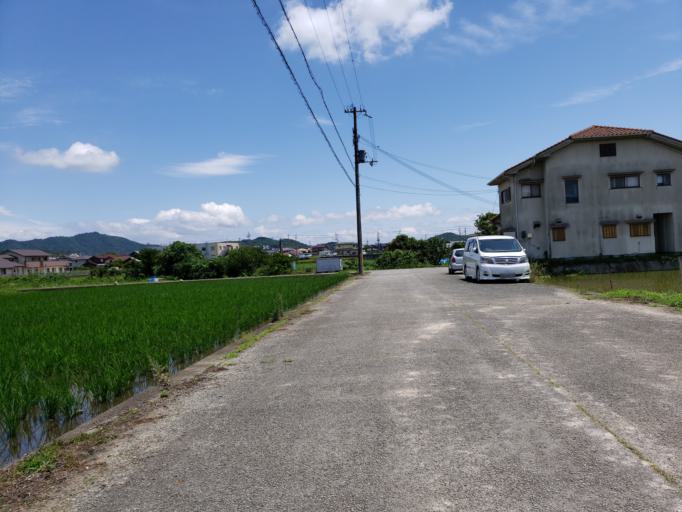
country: JP
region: Hyogo
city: Kakogawacho-honmachi
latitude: 34.8155
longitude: 134.8156
